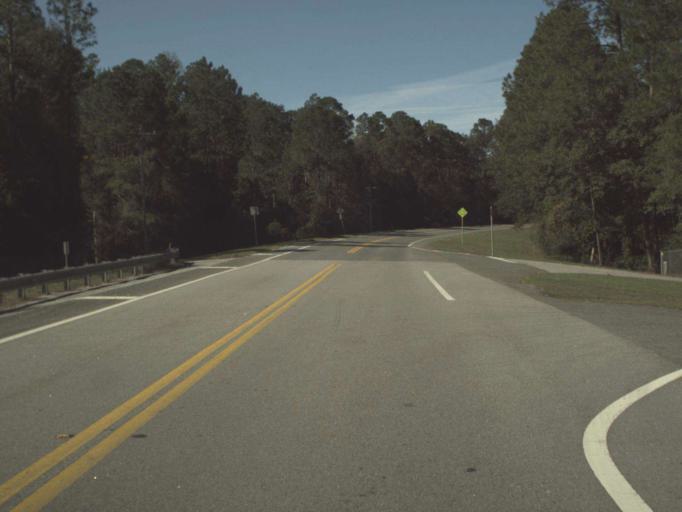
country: US
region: Florida
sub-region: Okaloosa County
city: Crestview
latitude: 30.8340
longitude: -86.7343
